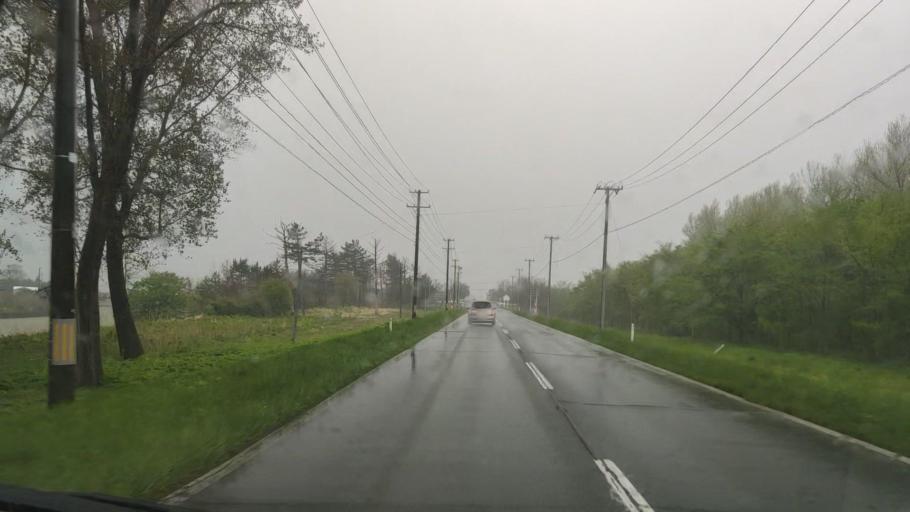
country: JP
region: Akita
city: Tenno
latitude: 39.9474
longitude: 139.9458
